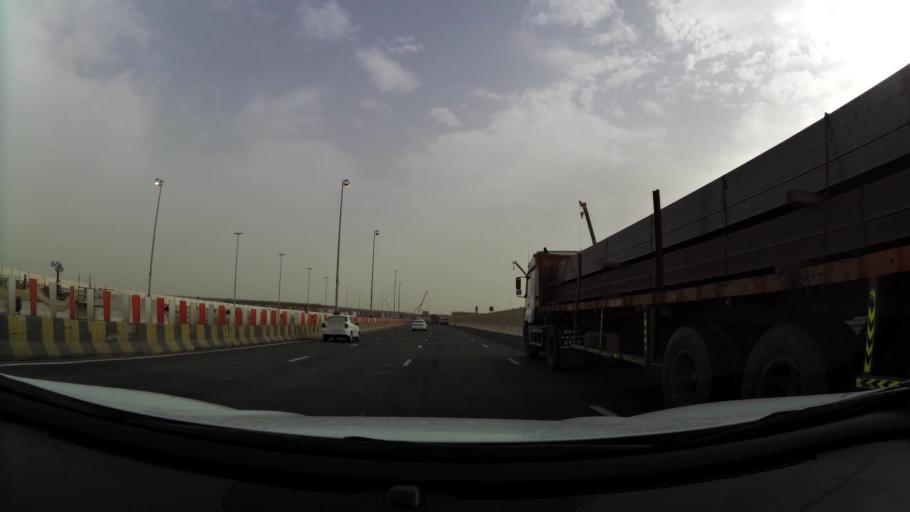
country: AE
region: Abu Dhabi
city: Abu Dhabi
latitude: 24.4529
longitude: 54.6224
